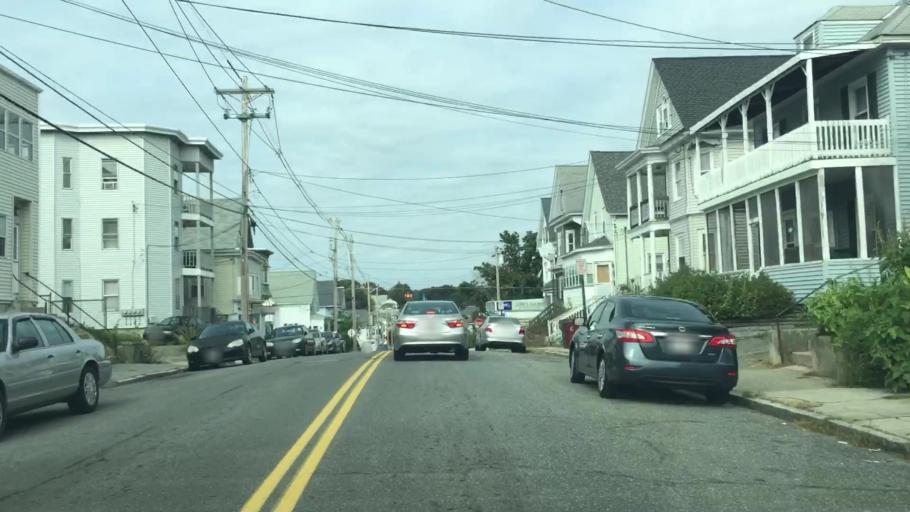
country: US
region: Massachusetts
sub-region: Middlesex County
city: Lowell
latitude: 42.6555
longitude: -71.3294
